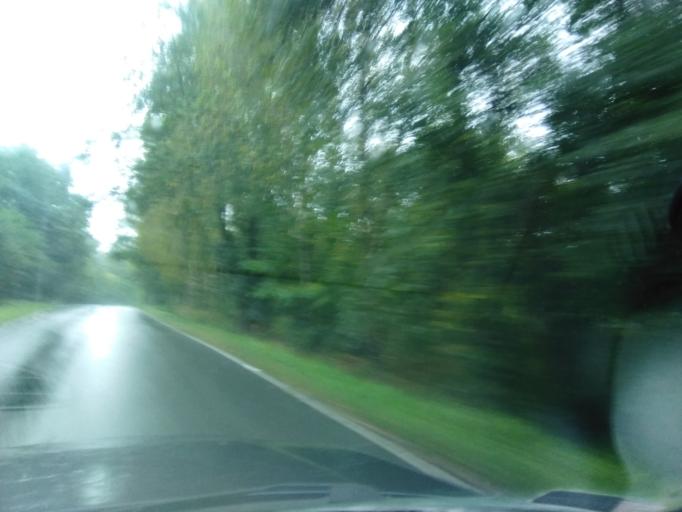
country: PL
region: Subcarpathian Voivodeship
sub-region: Powiat ropczycko-sedziszowski
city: Niedzwiada
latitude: 50.0400
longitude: 21.5444
